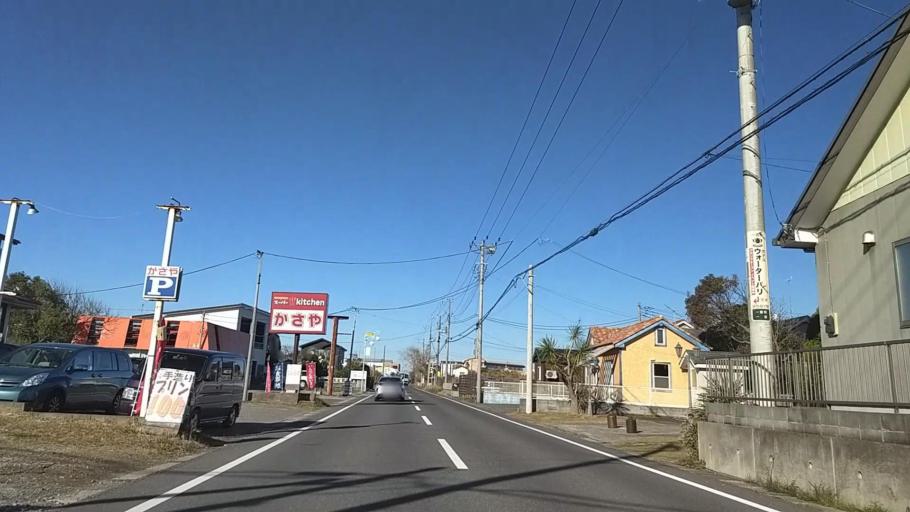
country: JP
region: Chiba
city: Mobara
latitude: 35.3577
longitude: 140.3885
